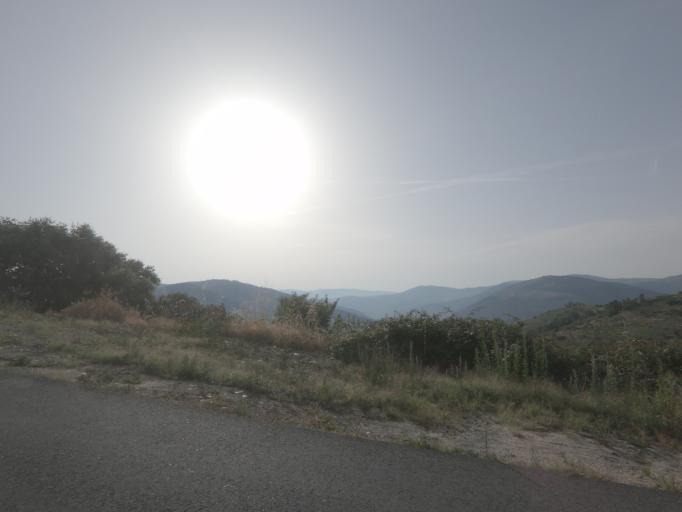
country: PT
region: Vila Real
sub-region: Sabrosa
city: Sabrosa
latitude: 41.2071
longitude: -7.5277
